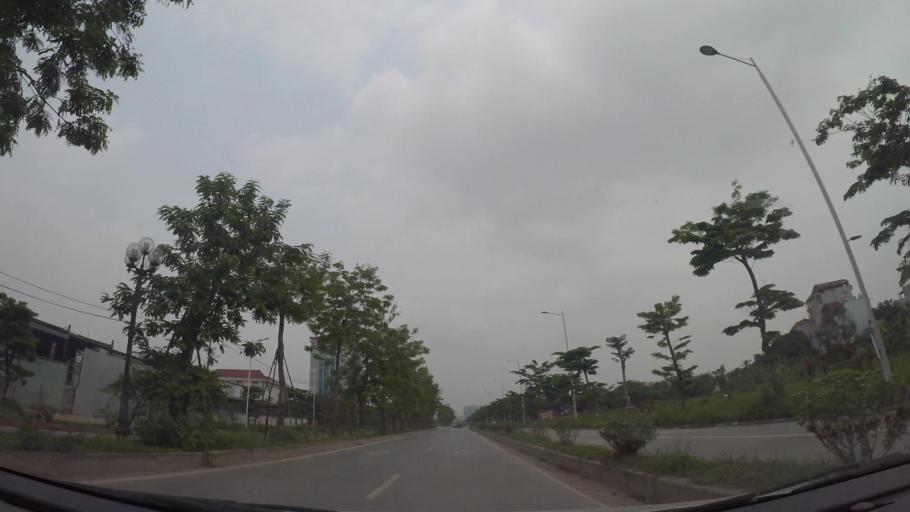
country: VN
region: Ha Noi
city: Cau Dien
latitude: 21.0402
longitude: 105.7403
